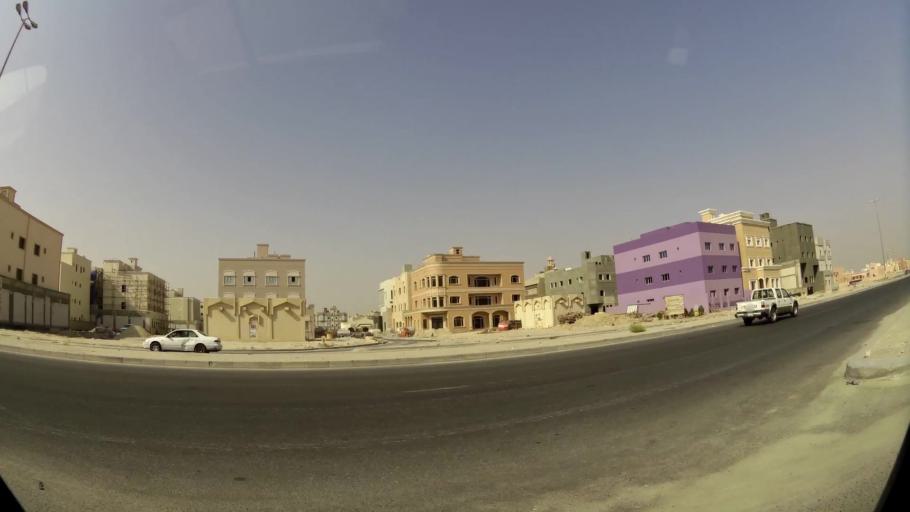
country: KW
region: Muhafazat al Jahra'
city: Al Jahra'
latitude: 29.3480
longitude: 47.7726
